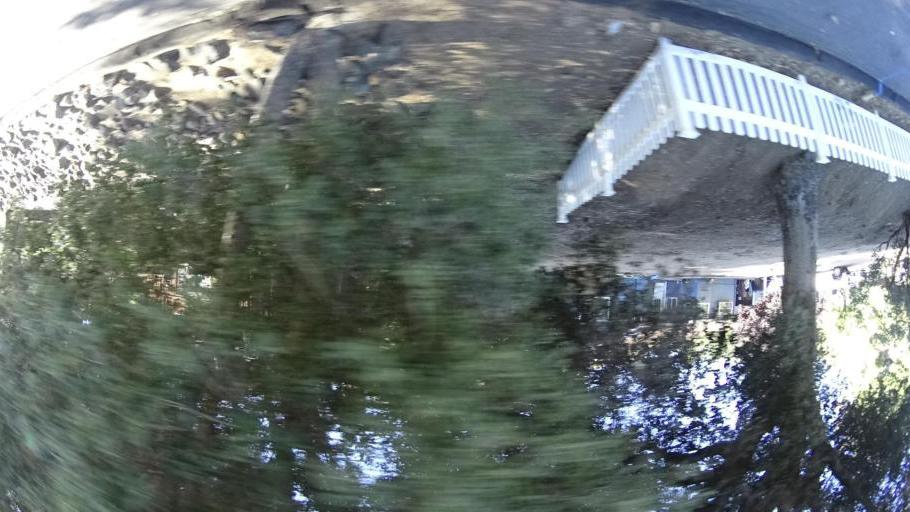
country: US
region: California
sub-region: San Diego County
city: Pine Valley
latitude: 32.8266
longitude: -116.5208
